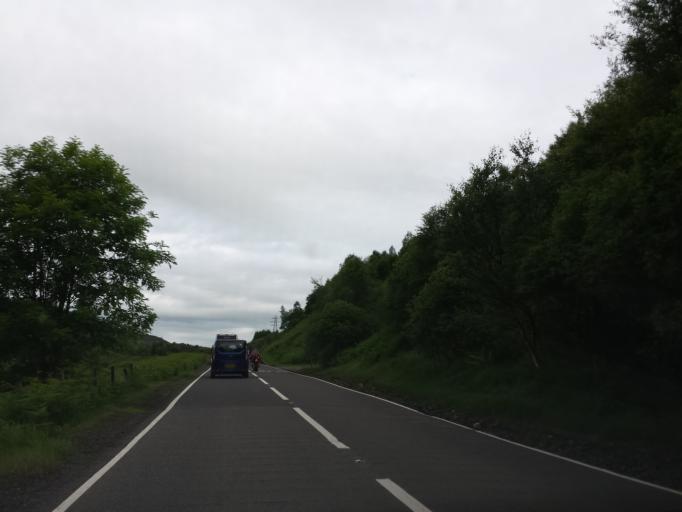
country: GB
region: Scotland
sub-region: Stirling
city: Callander
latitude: 56.4153
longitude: -4.3262
